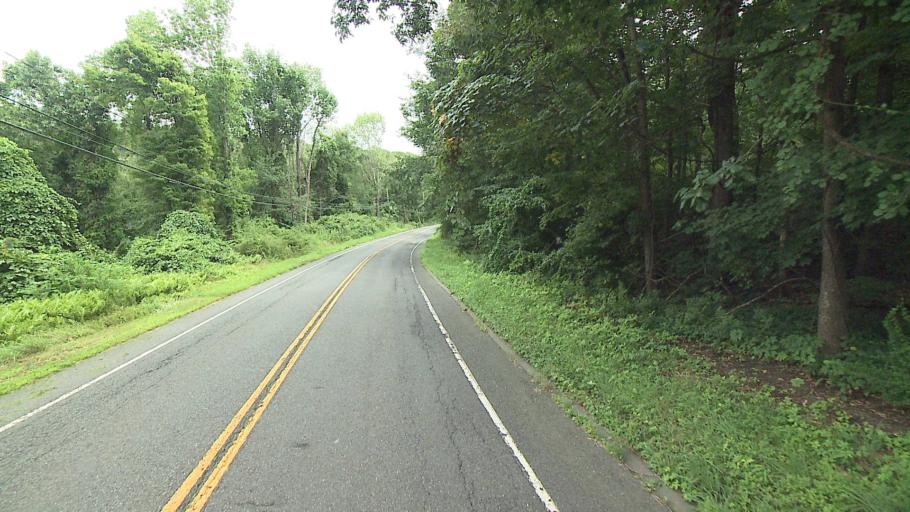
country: US
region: Connecticut
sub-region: Litchfield County
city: Woodbury
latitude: 41.5554
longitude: -73.2516
